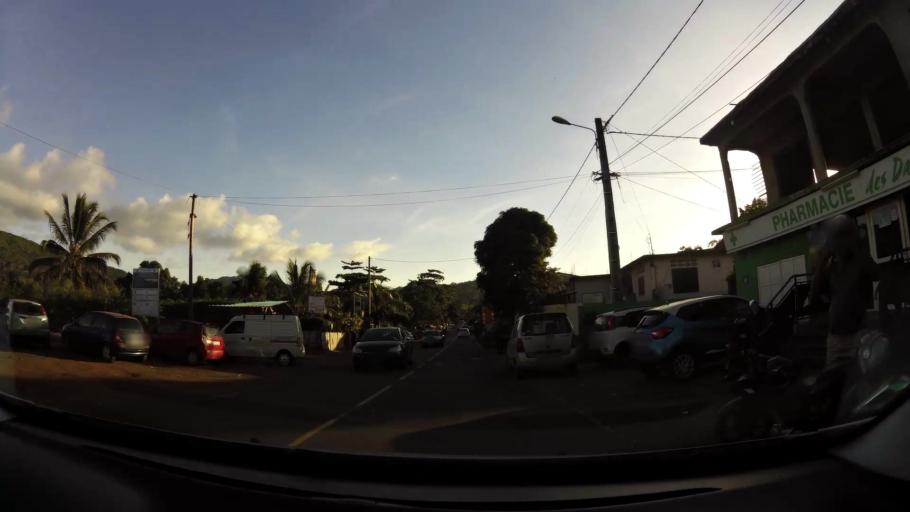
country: YT
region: Dembeni
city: Dembeni
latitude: -12.8369
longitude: 45.1765
